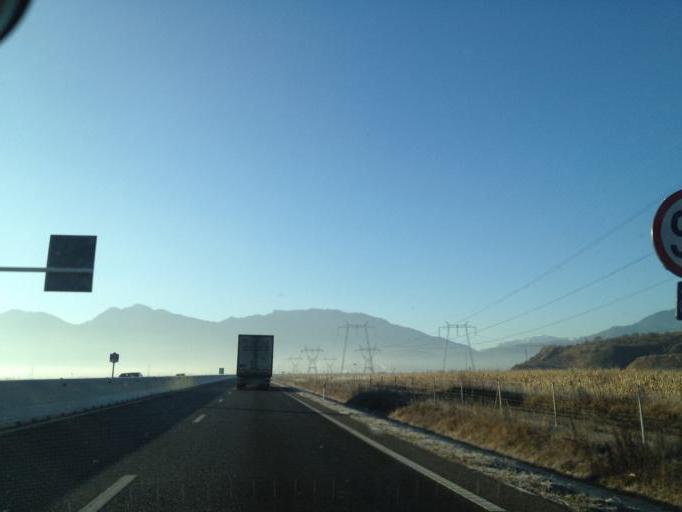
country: RO
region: Brasov
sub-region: Municipiul Sacele
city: Sacele
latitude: 45.6471
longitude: 25.6636
